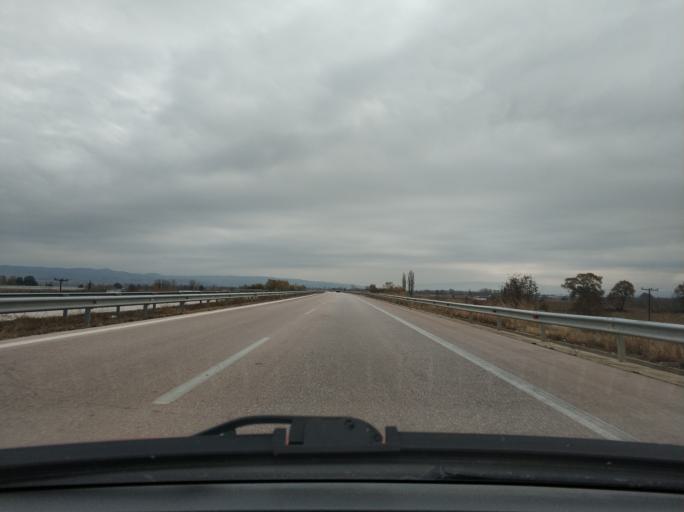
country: GR
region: Central Macedonia
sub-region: Nomos Thessalonikis
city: Lagkadas
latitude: 40.7260
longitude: 23.0776
